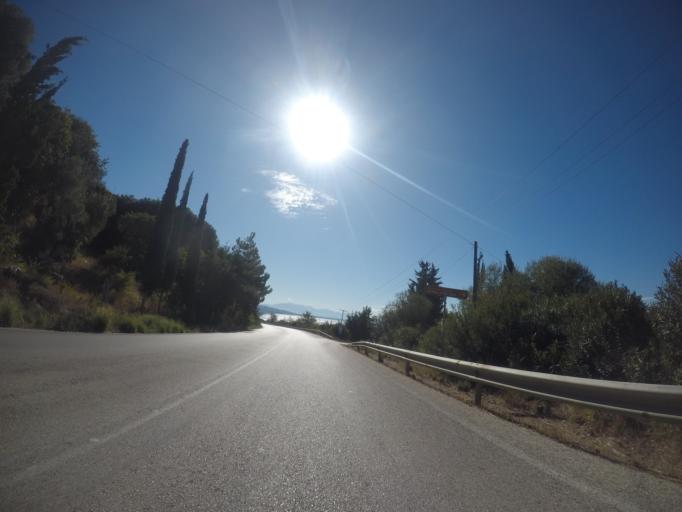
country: GR
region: Epirus
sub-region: Nomos Prevezis
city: Neos Oropos
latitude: 39.1042
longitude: 20.6380
